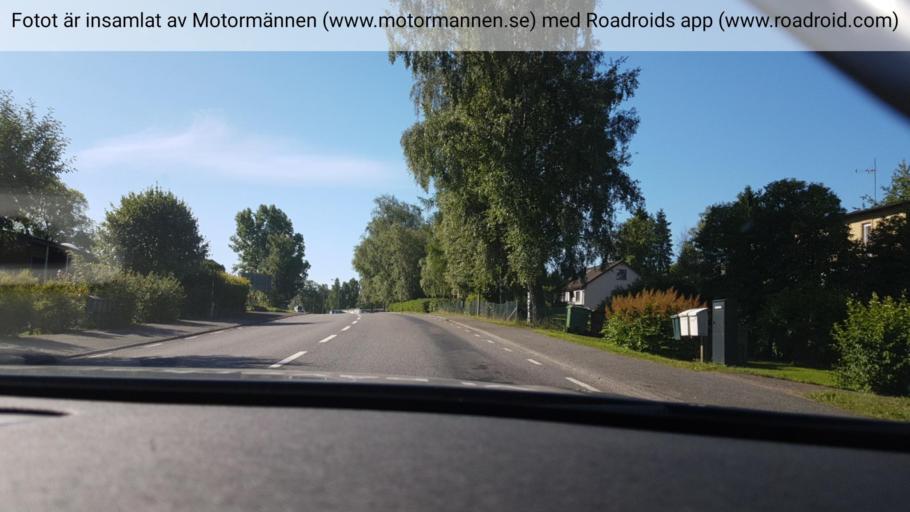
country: SE
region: Vaestra Goetaland
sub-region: Falkopings Kommun
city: Falkoeping
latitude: 58.0728
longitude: 13.5216
